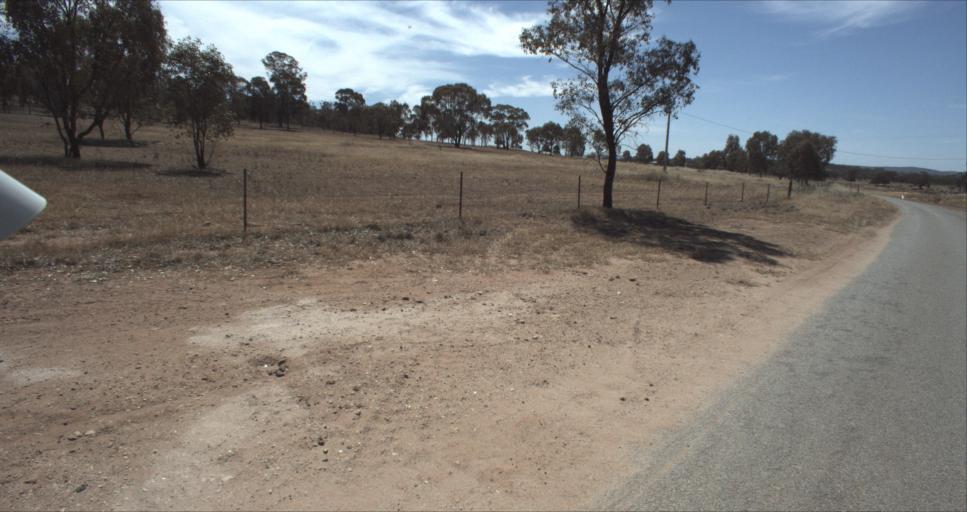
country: AU
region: New South Wales
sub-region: Leeton
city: Leeton
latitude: -34.6025
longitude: 146.4791
